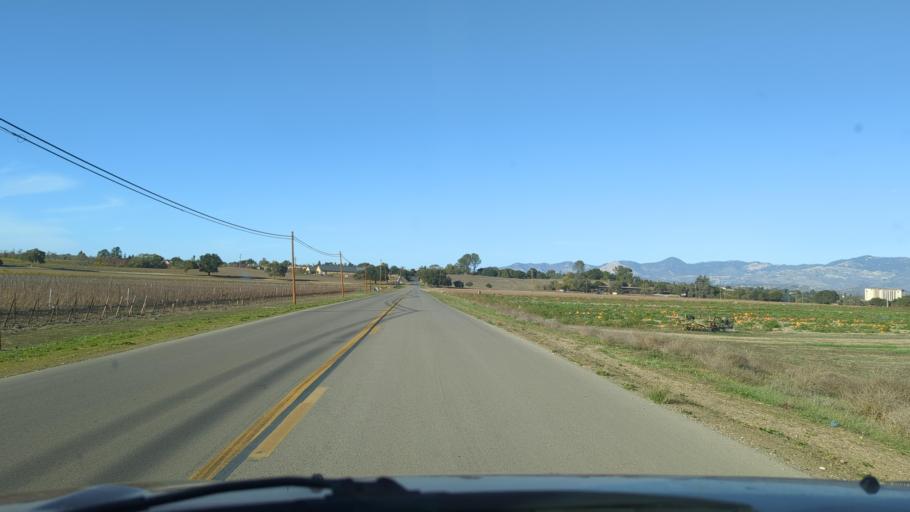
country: US
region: California
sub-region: Santa Barbara County
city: Santa Ynez
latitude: 34.5936
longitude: -120.0983
